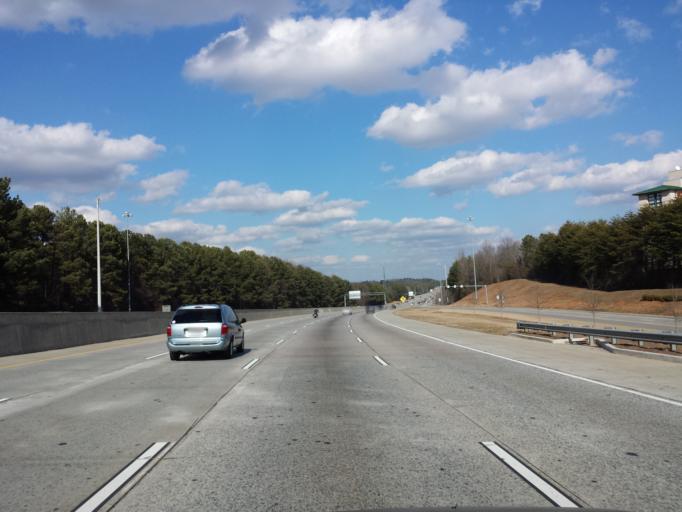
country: US
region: Georgia
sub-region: Fulton County
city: Alpharetta
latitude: 34.0891
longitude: -84.2610
